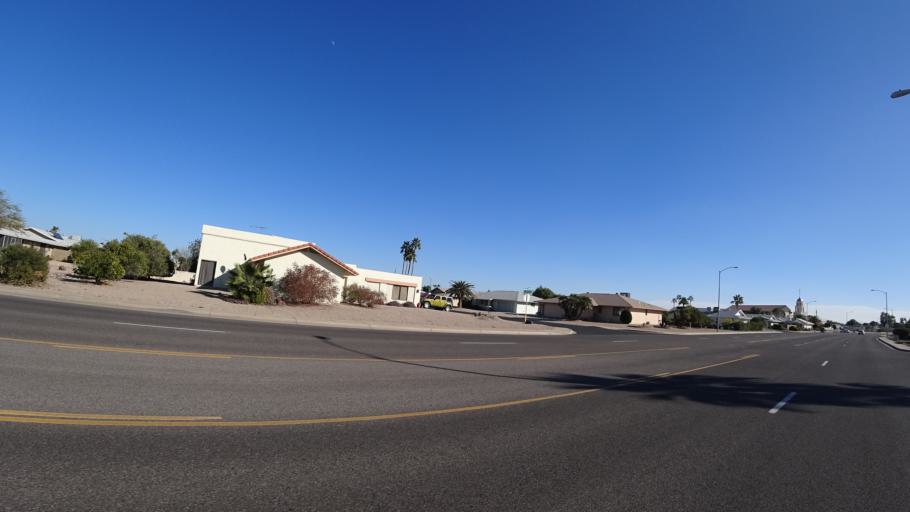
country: US
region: Arizona
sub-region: Maricopa County
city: Sun City West
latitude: 33.6606
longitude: -112.3314
